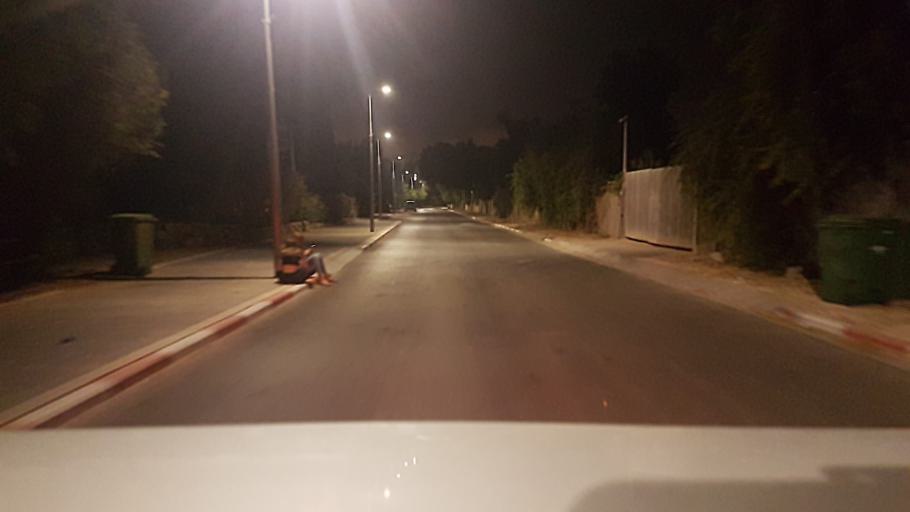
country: IL
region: Central District
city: Nehalim
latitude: 32.0746
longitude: 34.9232
